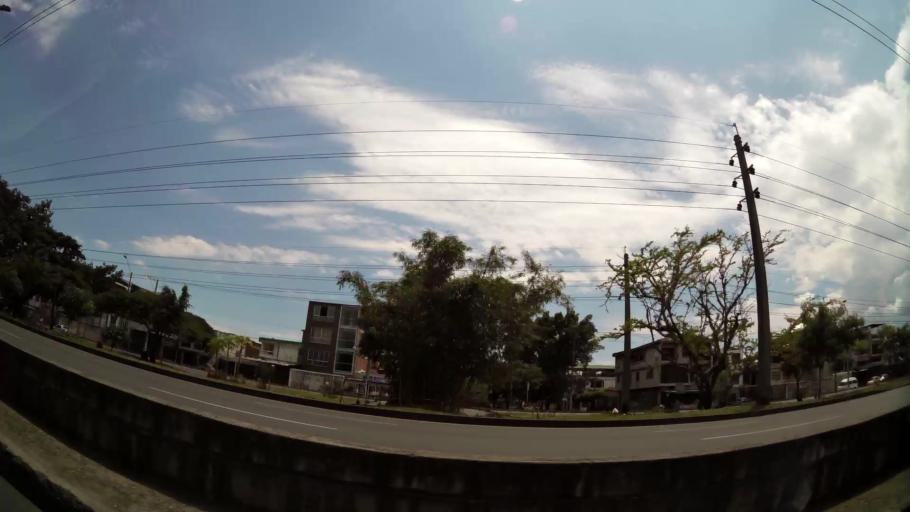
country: CO
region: Valle del Cauca
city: Cali
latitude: 3.4372
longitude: -76.5116
